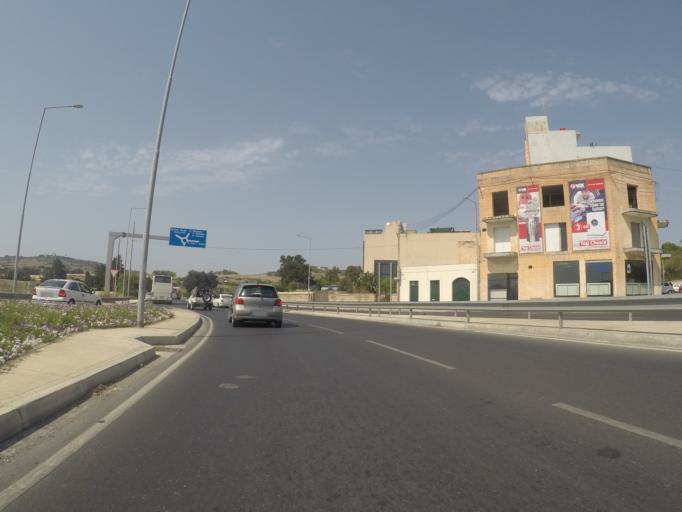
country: MT
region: Saint Paul's Bay
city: San Pawl il-Bahar
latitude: 35.9449
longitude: 14.4123
